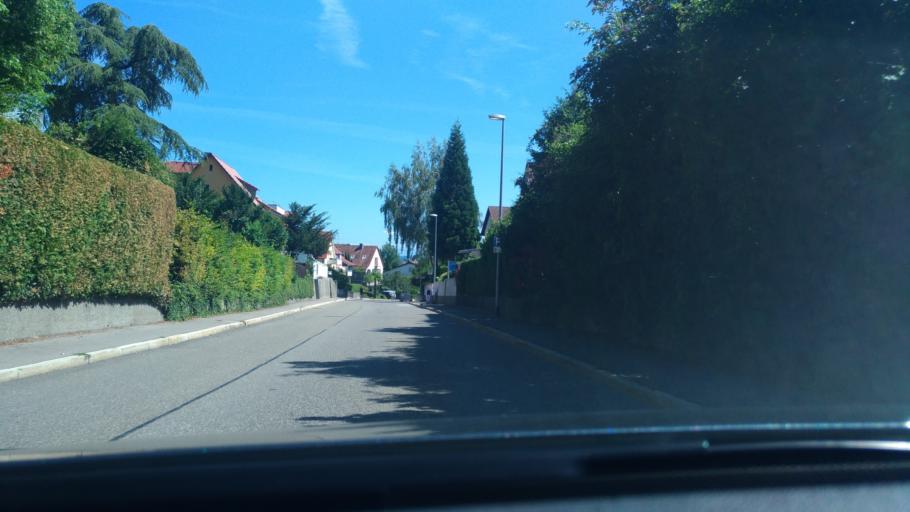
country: DE
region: Baden-Wuerttemberg
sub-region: Tuebingen Region
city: Uberlingen
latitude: 47.7729
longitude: 9.1547
